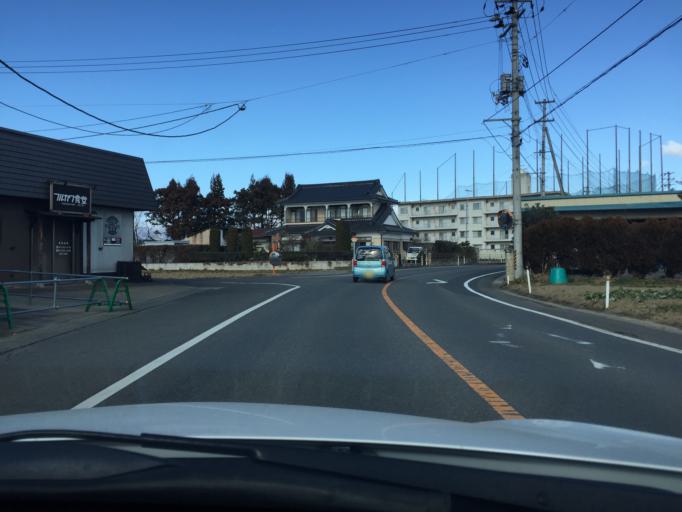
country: JP
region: Fukushima
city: Koriyama
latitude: 37.3998
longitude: 140.3163
